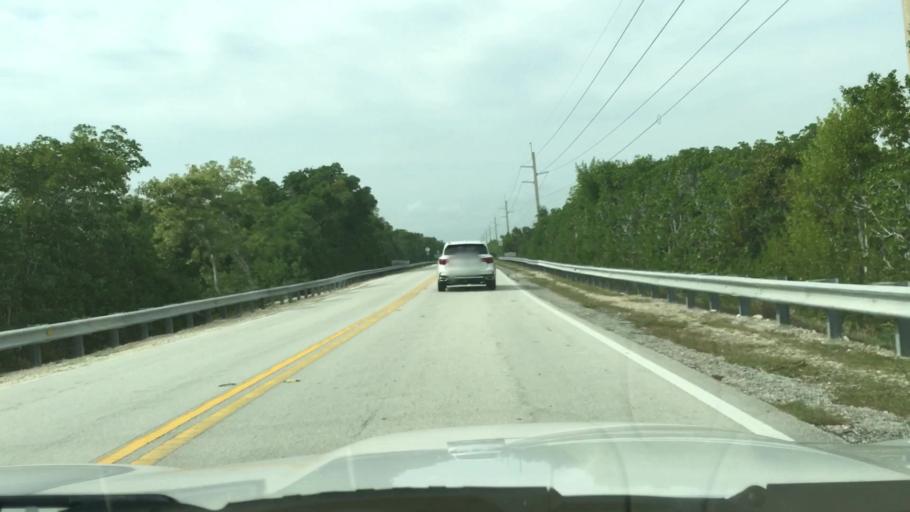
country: US
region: Florida
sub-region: Monroe County
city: North Key Largo
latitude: 25.2797
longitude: -80.3438
